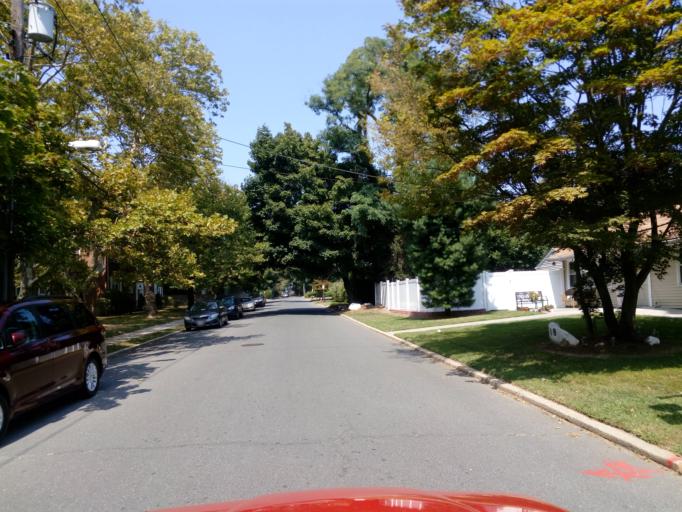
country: US
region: New York
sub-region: Nassau County
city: Glen Cove
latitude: 40.8729
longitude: -73.6353
